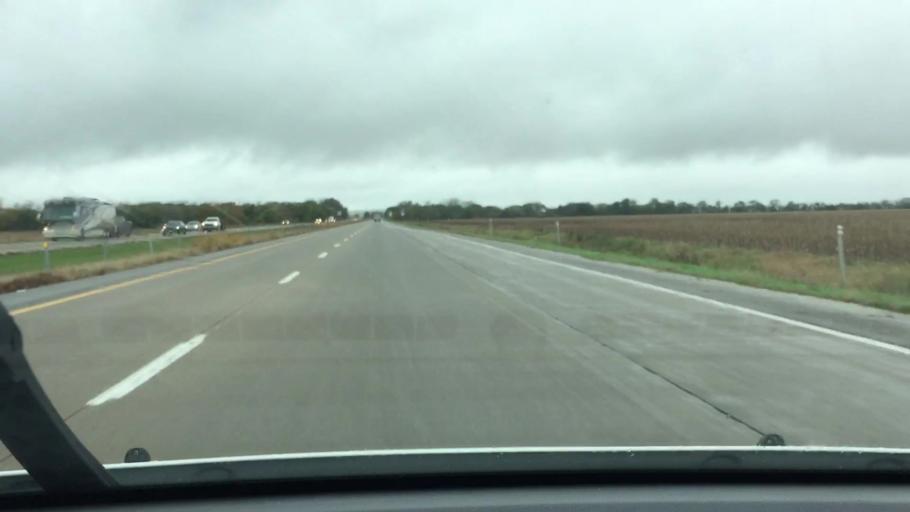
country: US
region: Iowa
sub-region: Jasper County
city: Colfax
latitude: 41.6928
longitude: -93.1853
